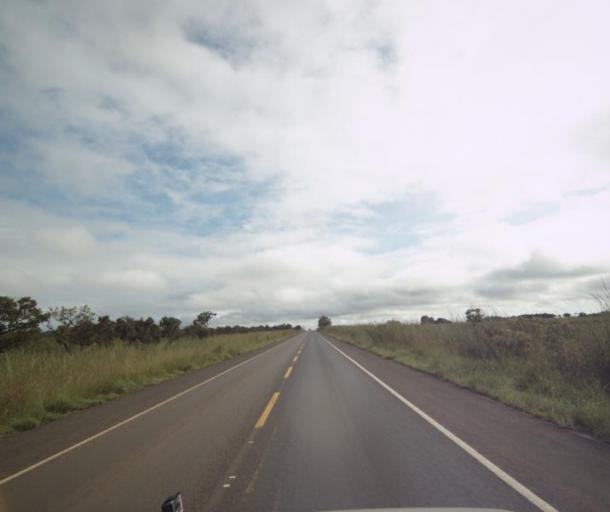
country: BR
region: Goias
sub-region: Padre Bernardo
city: Padre Bernardo
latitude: -15.3618
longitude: -48.6463
